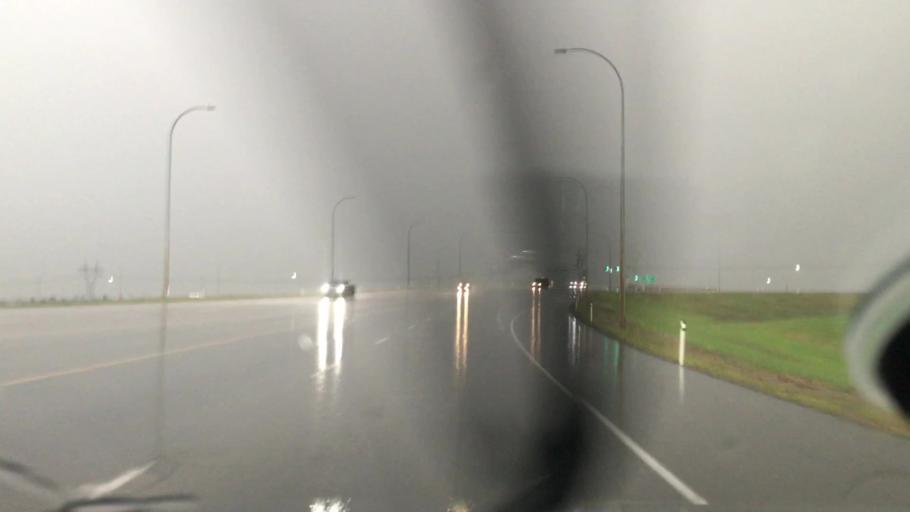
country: CA
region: Alberta
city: Devon
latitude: 53.4423
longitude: -113.6049
